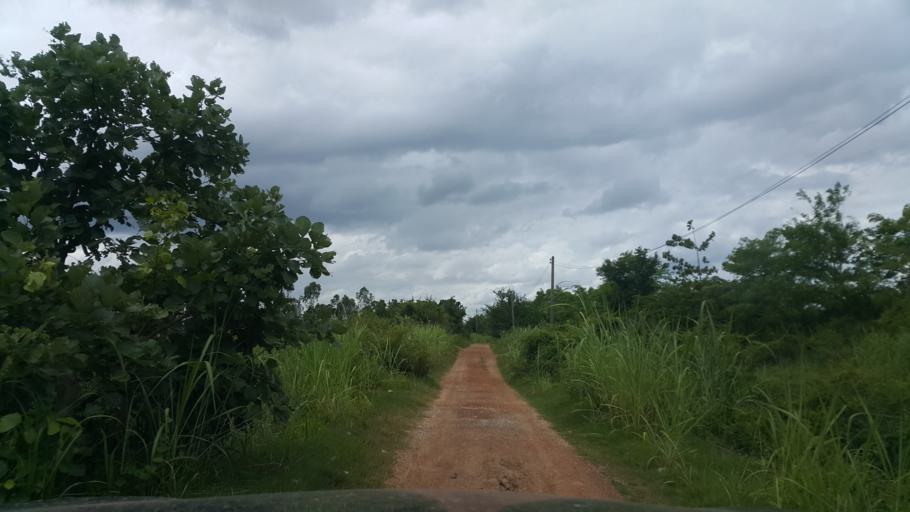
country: TH
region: Sukhothai
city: Sukhothai
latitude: 17.0236
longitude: 99.7973
